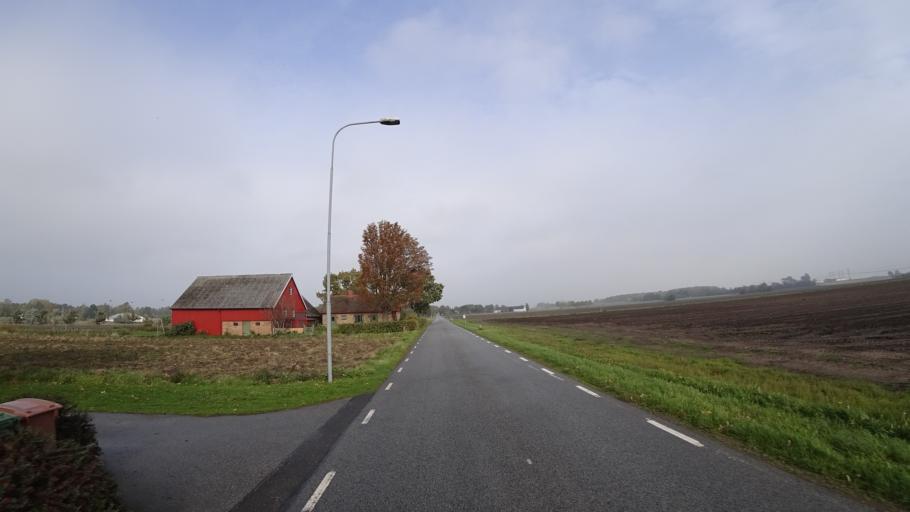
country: SE
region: Skane
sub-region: Kavlinge Kommun
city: Hofterup
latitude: 55.7903
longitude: 12.9838
